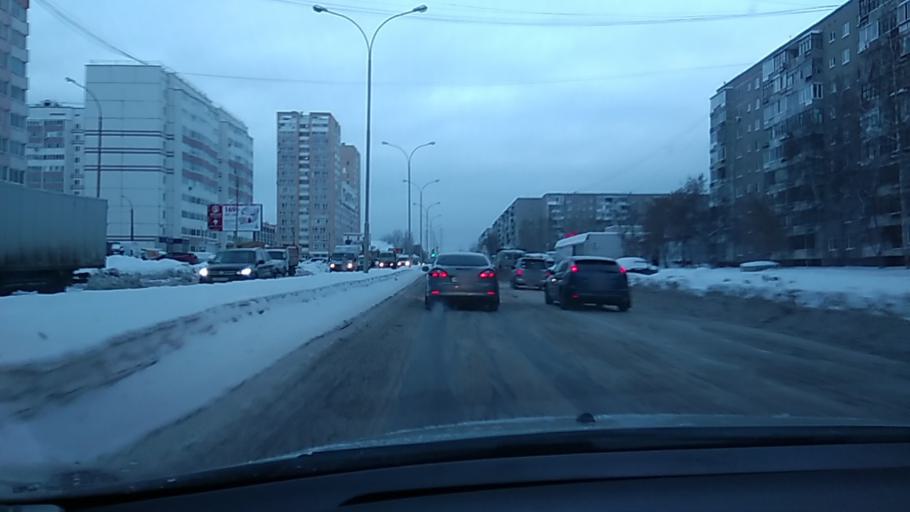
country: RU
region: Sverdlovsk
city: Yekaterinburg
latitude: 56.9060
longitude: 60.5886
